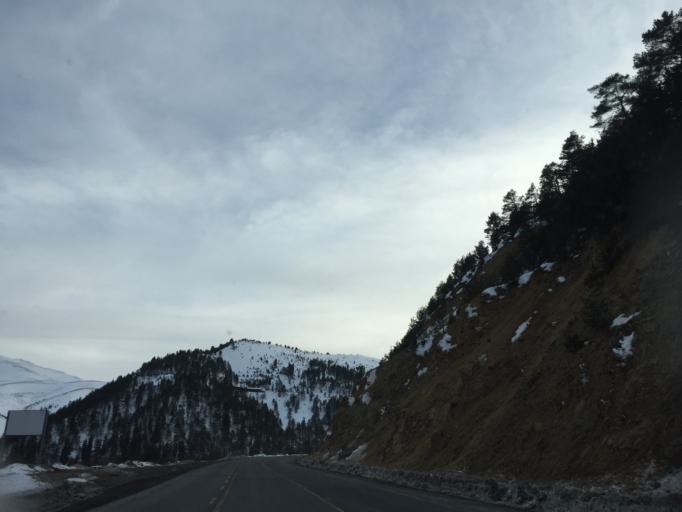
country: TR
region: Gumushane
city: Yaglidere
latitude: 40.6613
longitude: 39.4143
